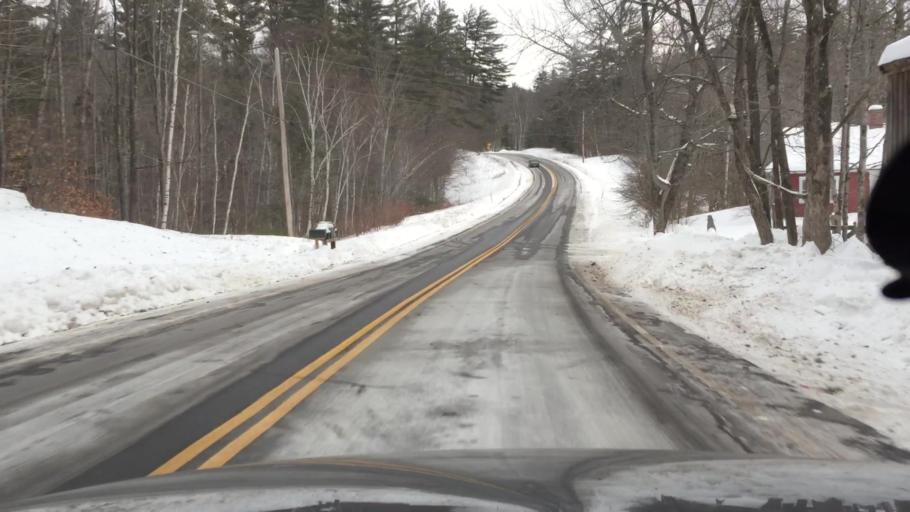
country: US
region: New Hampshire
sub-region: Carroll County
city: Sandwich
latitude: 43.7991
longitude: -71.5045
